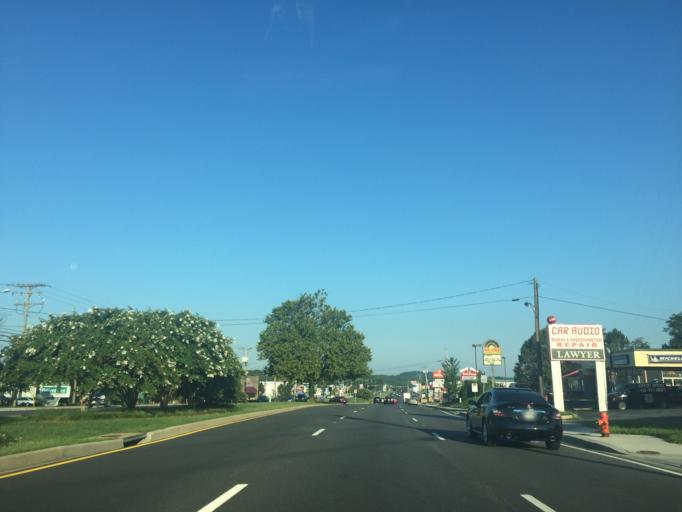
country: US
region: Maryland
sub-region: Baltimore County
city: Catonsville
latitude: 39.2840
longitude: -76.7552
